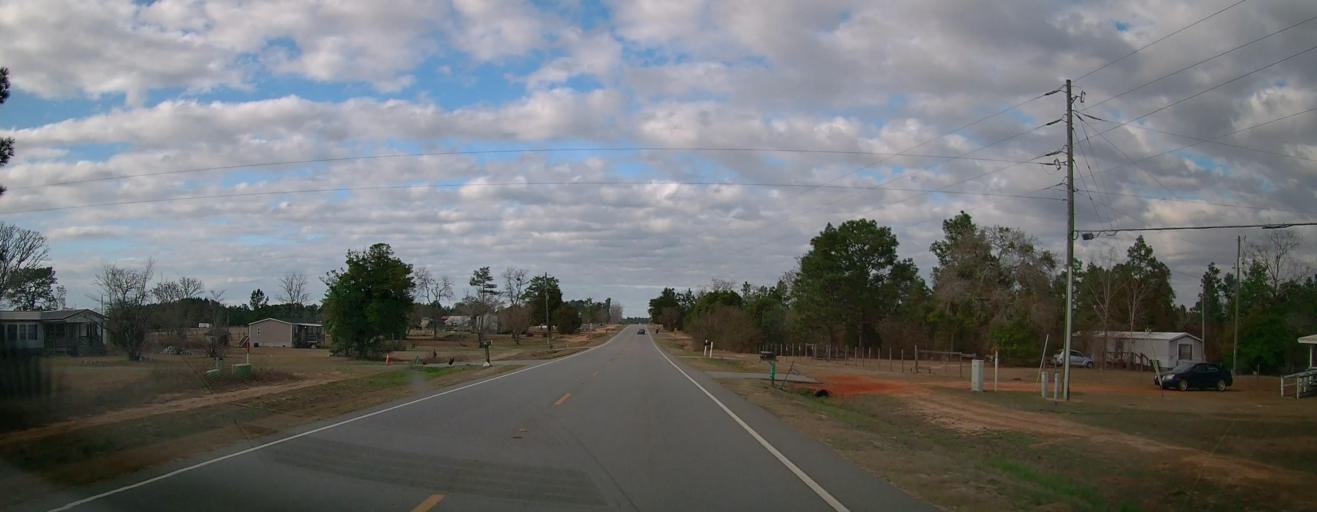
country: US
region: Georgia
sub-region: Marion County
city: Buena Vista
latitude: 32.4602
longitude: -84.5382
